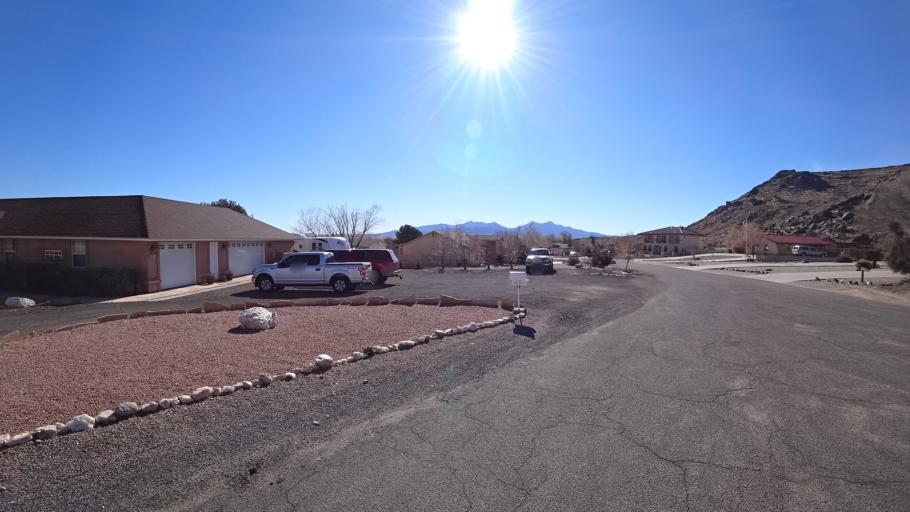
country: US
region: Arizona
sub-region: Mohave County
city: New Kingman-Butler
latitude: 35.2677
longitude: -114.0507
